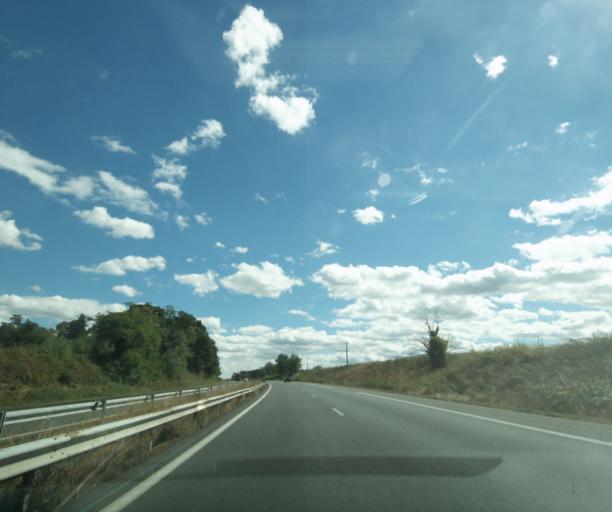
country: FR
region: Aquitaine
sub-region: Departement de la Gironde
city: Preignac
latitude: 44.5635
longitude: -0.3002
